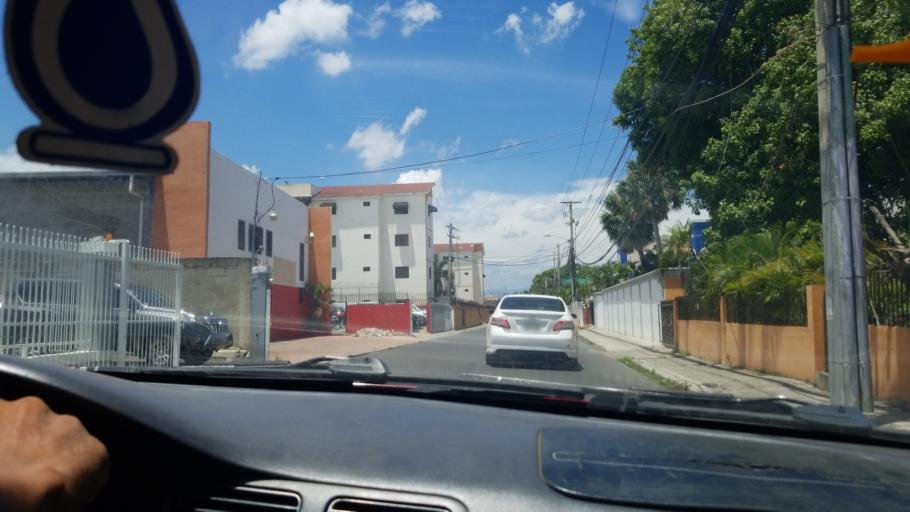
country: DO
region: Santiago
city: Santiago de los Caballeros
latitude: 19.4756
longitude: -70.6900
